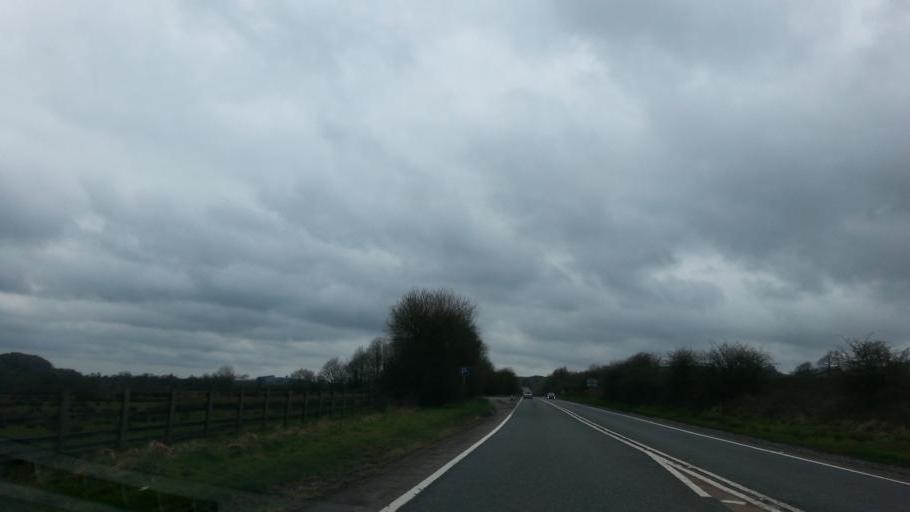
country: GB
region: England
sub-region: Devon
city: South Molton
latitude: 51.0326
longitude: -3.8403
